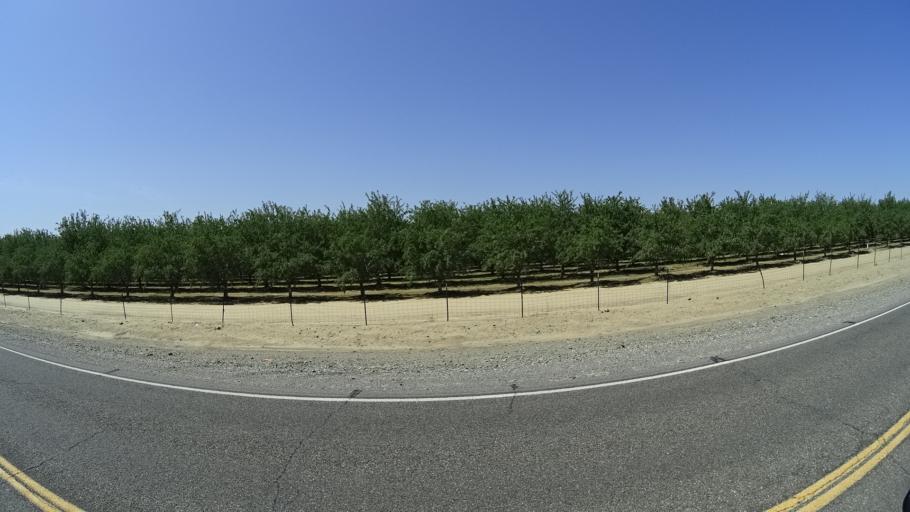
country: US
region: California
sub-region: Glenn County
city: Orland
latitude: 39.6756
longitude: -122.1969
